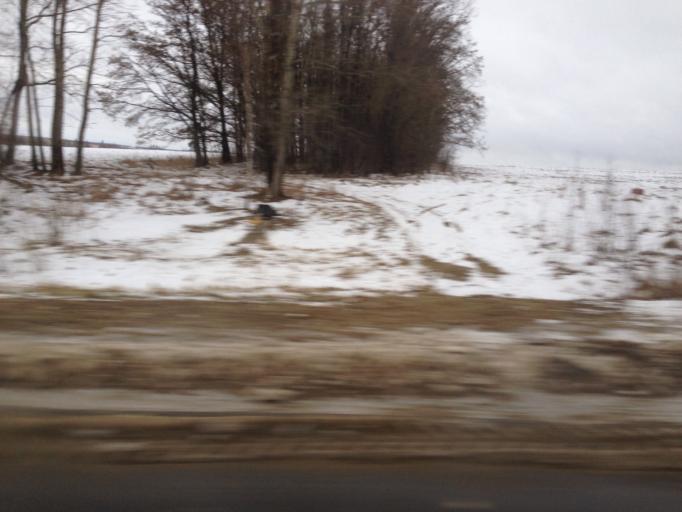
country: RU
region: Tula
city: Bolokhovo
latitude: 54.0390
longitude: 37.8709
